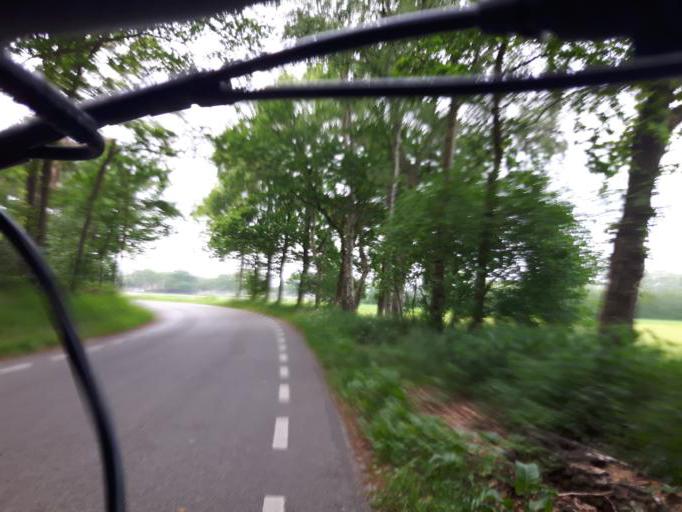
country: NL
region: North Brabant
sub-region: Gemeente Bergen op Zoom
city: Lepelstraat
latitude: 51.5306
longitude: 4.2997
